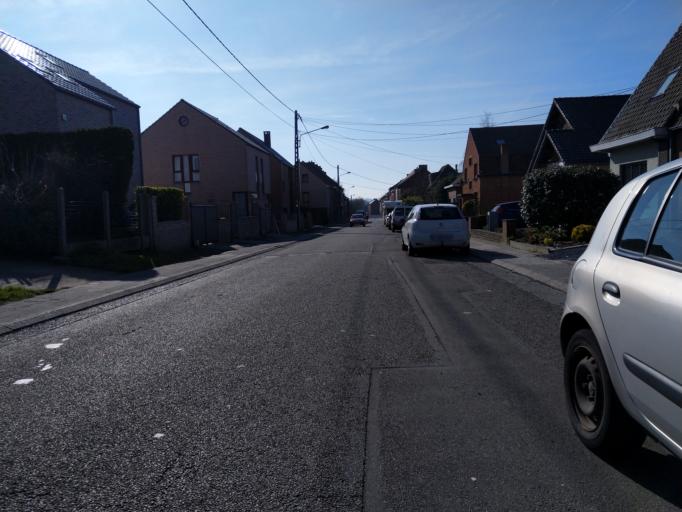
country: BE
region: Wallonia
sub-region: Province du Hainaut
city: Chasse Royale
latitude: 50.4374
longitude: 3.9361
